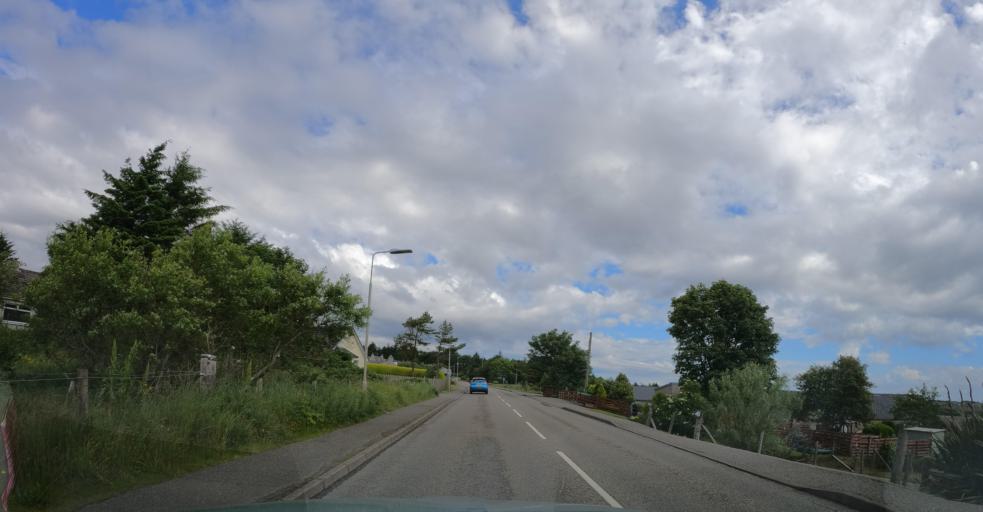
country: GB
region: Scotland
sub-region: Eilean Siar
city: Isle of Lewis
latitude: 58.2325
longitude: -6.3902
